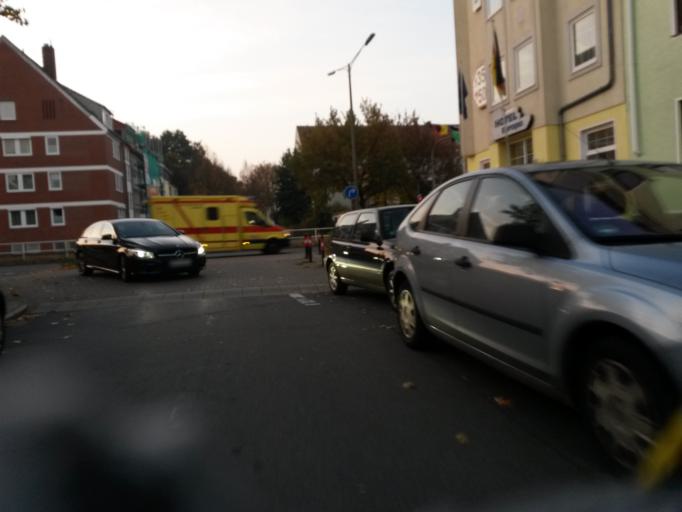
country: DE
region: Bremen
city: Bremen
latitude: 53.0647
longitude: 8.8706
